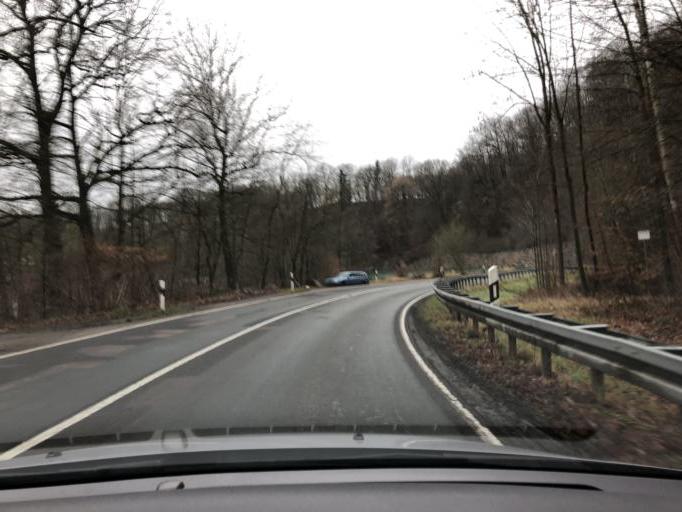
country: DE
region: Saxony
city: Niederstriegis
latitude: 51.0907
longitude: 13.1357
